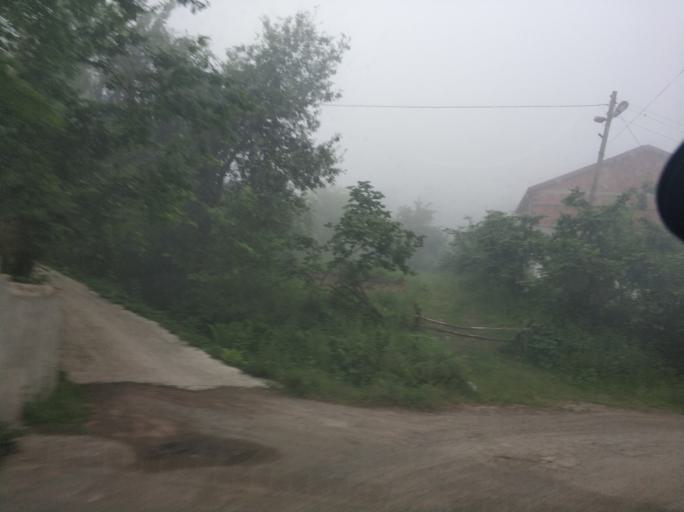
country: TR
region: Giresun
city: Nefsipiraziz
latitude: 40.8871
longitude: 38.0814
